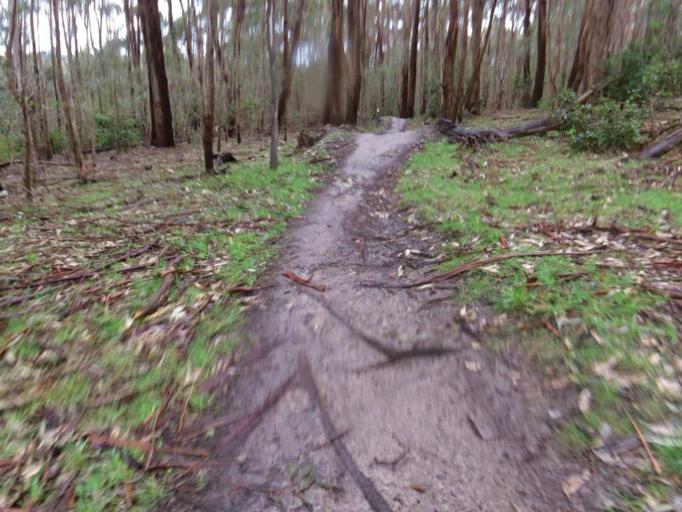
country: AU
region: Victoria
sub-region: Yarra Ranges
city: Lysterfield
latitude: -37.9420
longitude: 145.2798
